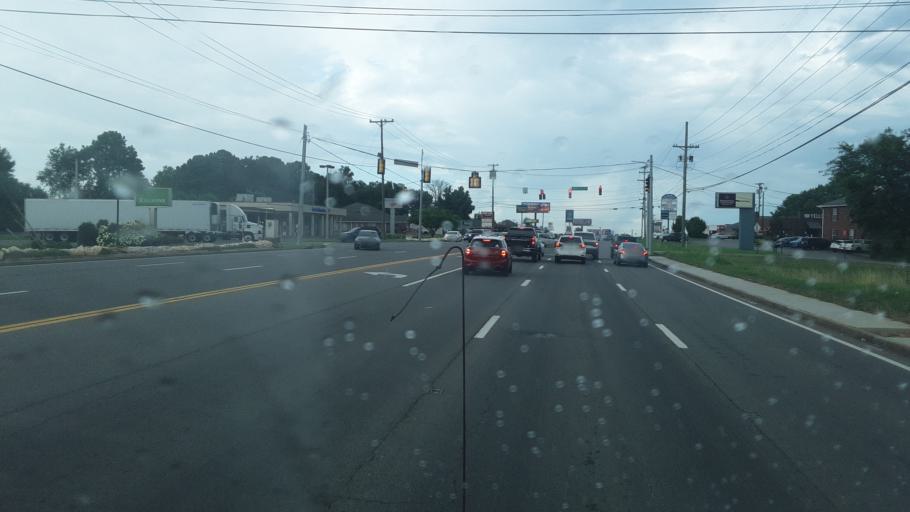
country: US
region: Tennessee
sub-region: Montgomery County
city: Clarksville
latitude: 36.5760
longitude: -87.3018
